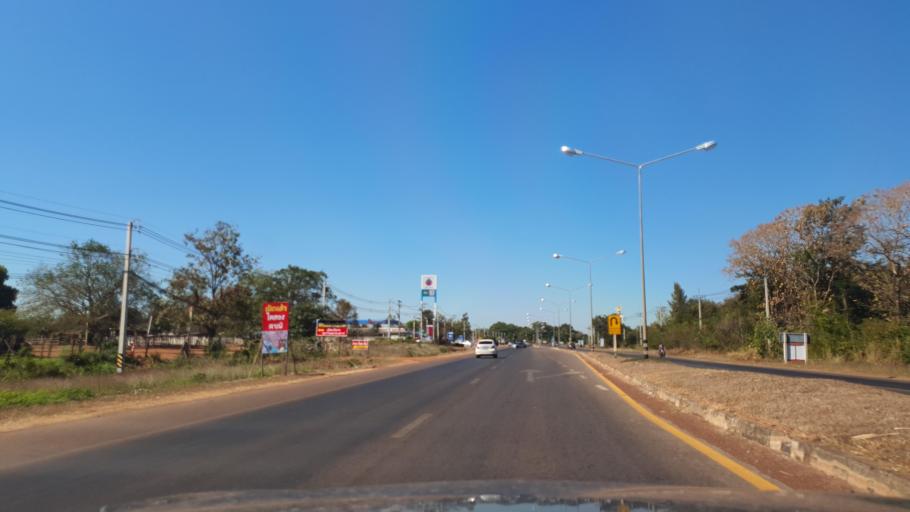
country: TH
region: Sakon Nakhon
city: Sakon Nakhon
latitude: 17.2568
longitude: 104.1688
